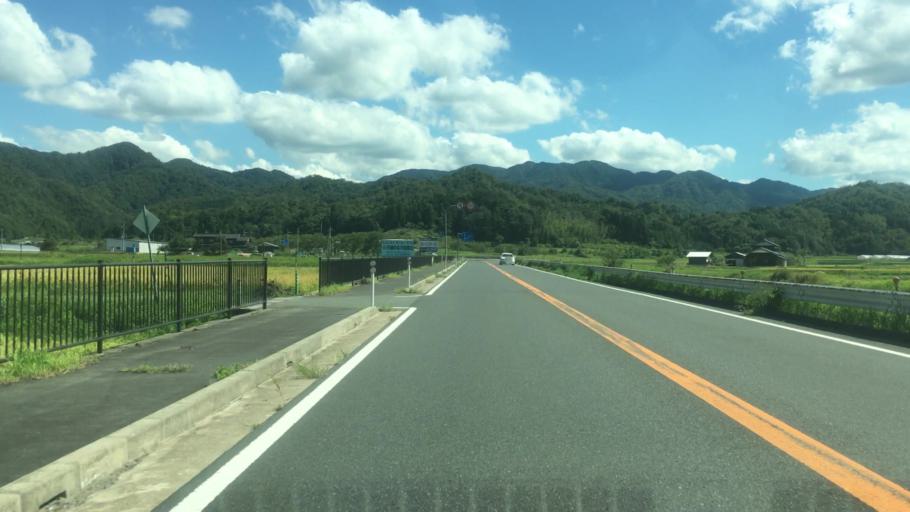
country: JP
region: Hyogo
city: Toyooka
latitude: 35.5770
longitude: 134.9742
